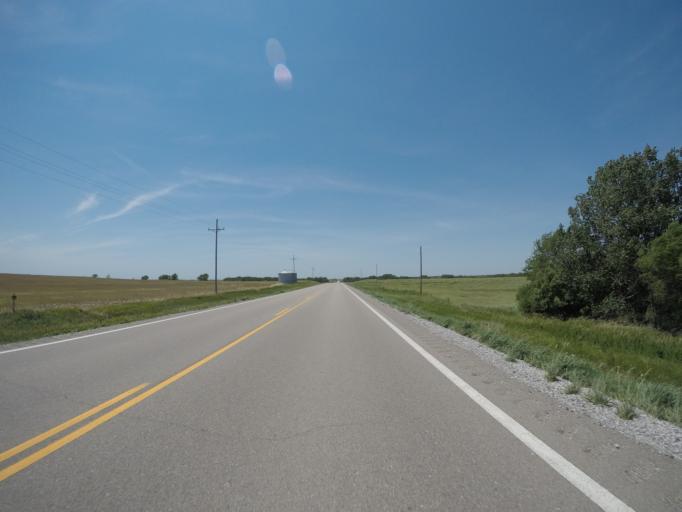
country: US
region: Kansas
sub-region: Dickinson County
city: Solomon
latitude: 39.0306
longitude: -97.3442
